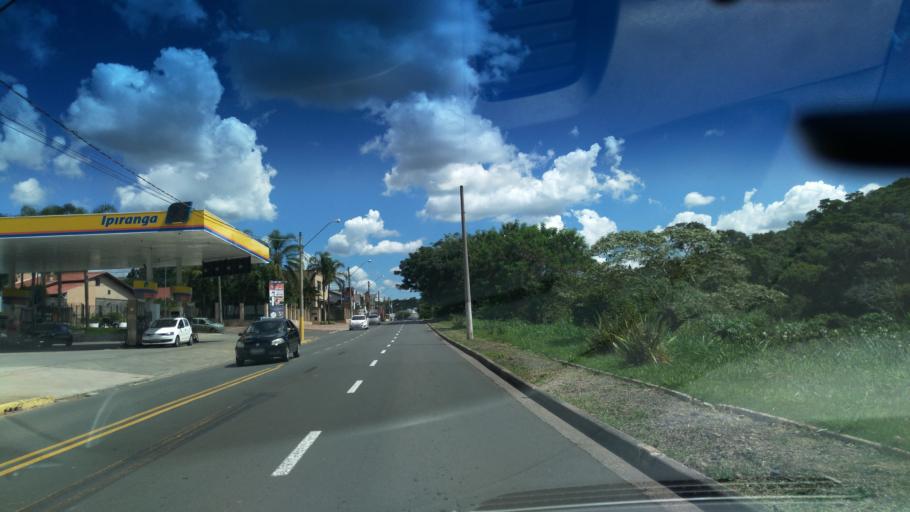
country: BR
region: Sao Paulo
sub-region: Valinhos
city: Valinhos
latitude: -22.9678
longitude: -47.0109
